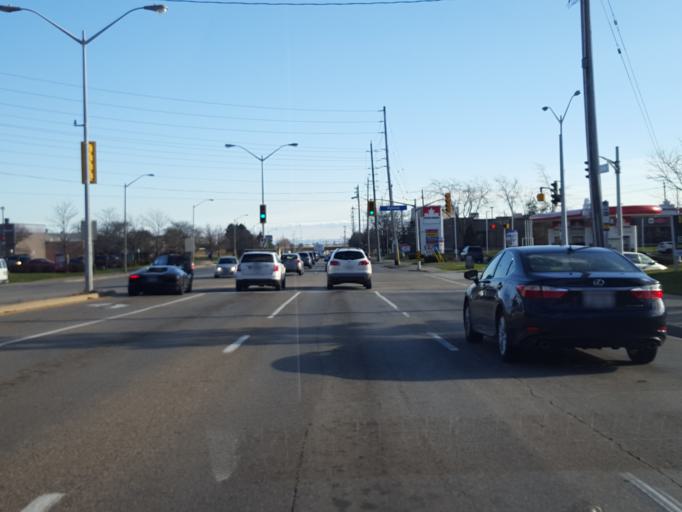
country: CA
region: Ontario
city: Burlington
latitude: 43.3721
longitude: -79.7963
